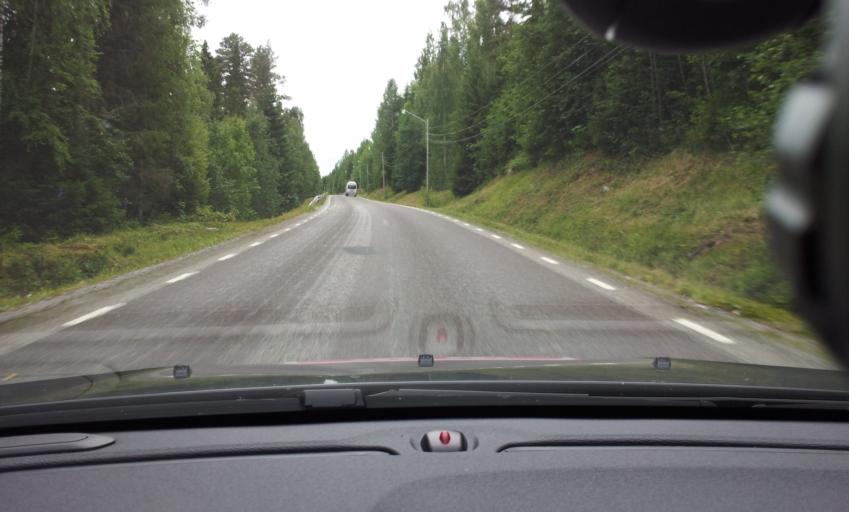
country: SE
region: Jaemtland
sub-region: Braecke Kommun
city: Braecke
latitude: 63.0321
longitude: 15.2465
